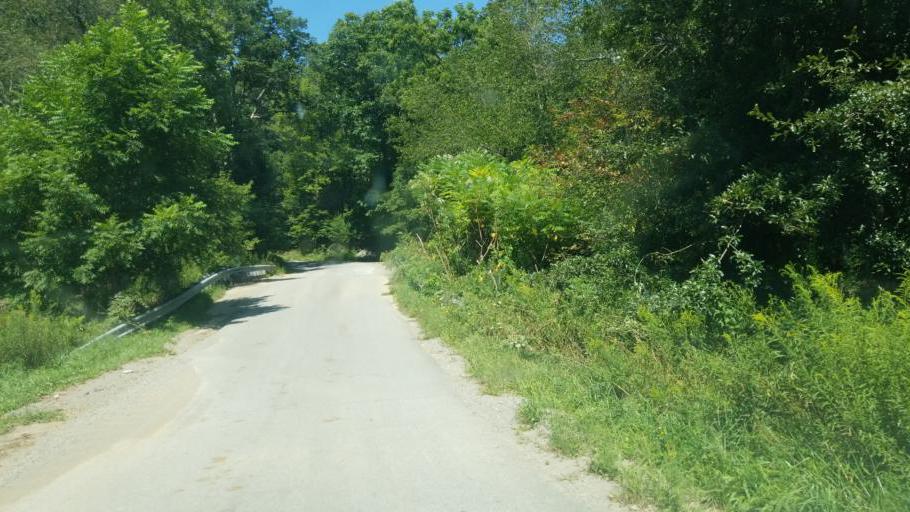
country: US
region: Pennsylvania
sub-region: Clarion County
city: Knox
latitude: 41.1961
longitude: -79.6132
